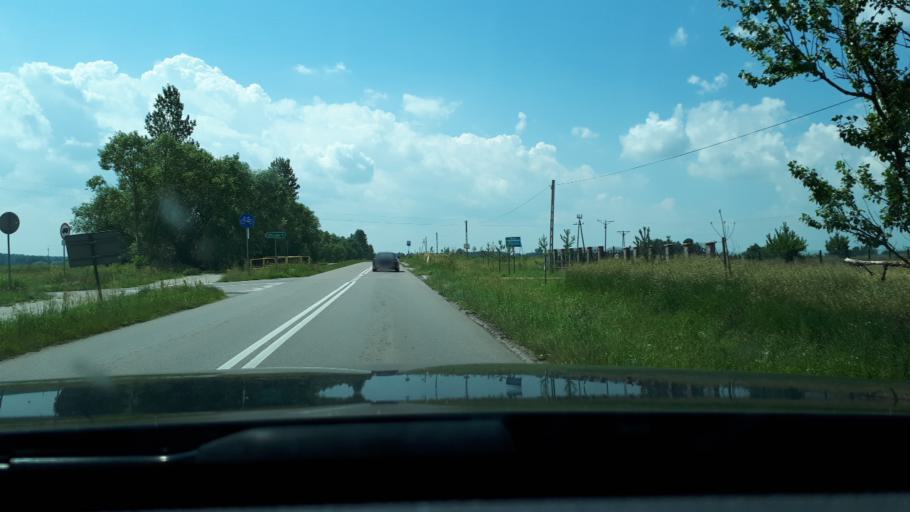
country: PL
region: Podlasie
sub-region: Powiat bialostocki
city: Choroszcz
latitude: 53.1306
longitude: 23.0329
